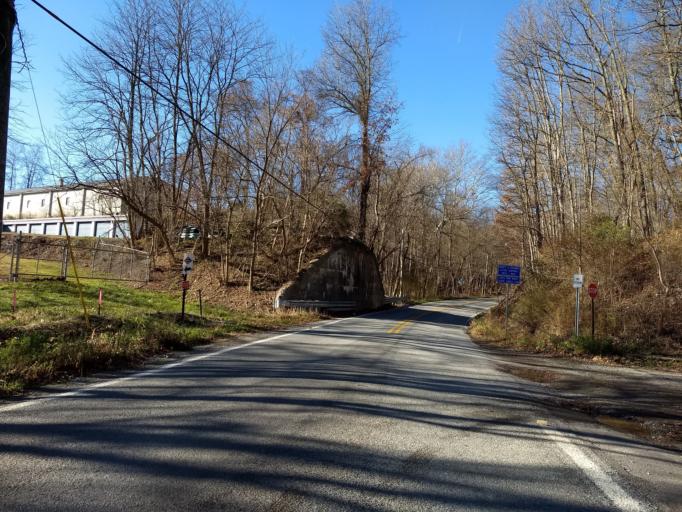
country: US
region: Pennsylvania
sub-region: Allegheny County
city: South Park Township
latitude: 40.2895
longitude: -80.0085
